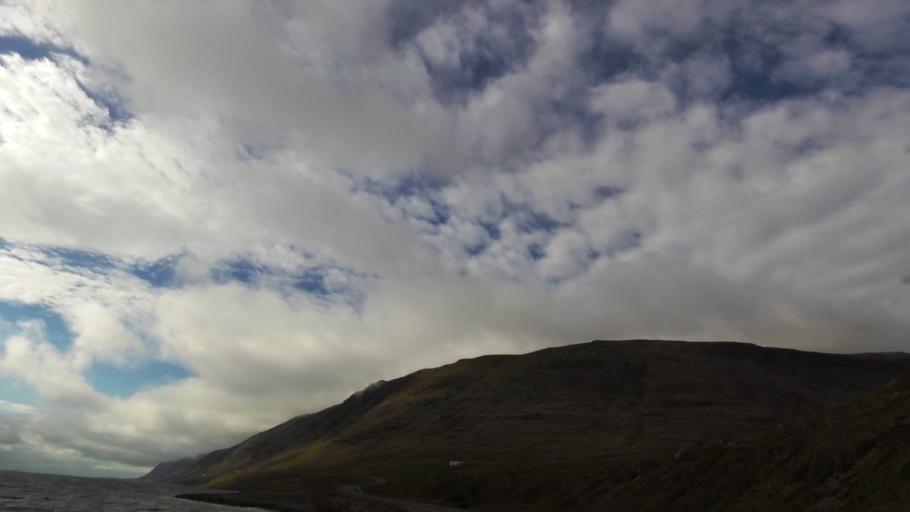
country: IS
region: West
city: Olafsvik
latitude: 65.5489
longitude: -23.8877
